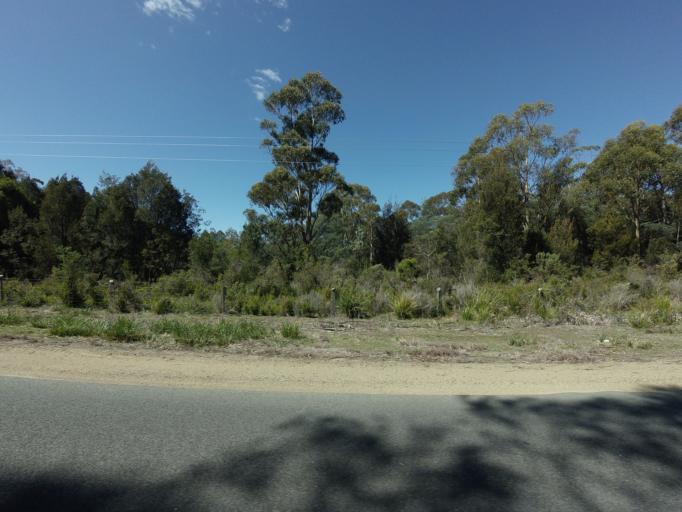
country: AU
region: Tasmania
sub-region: Break O'Day
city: St Helens
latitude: -41.6725
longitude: 148.2791
